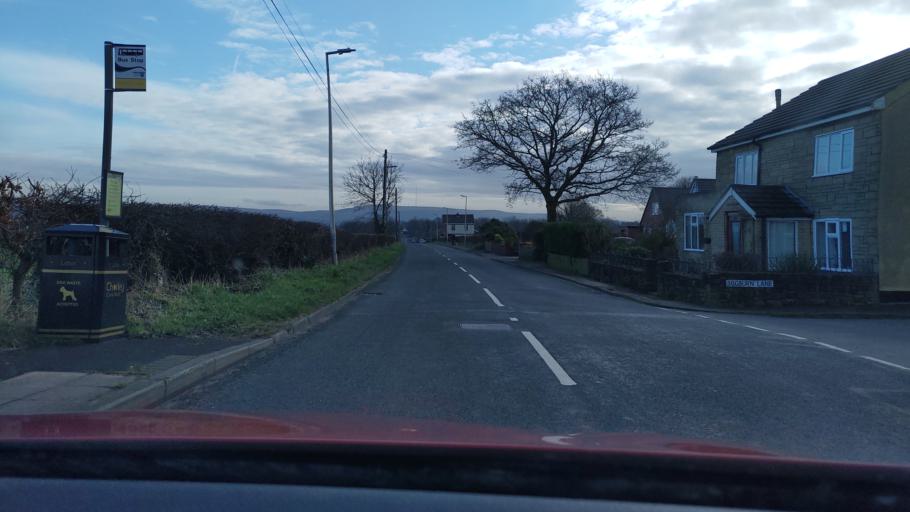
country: GB
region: England
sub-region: Lancashire
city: Coppull
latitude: 53.6099
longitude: -2.6701
